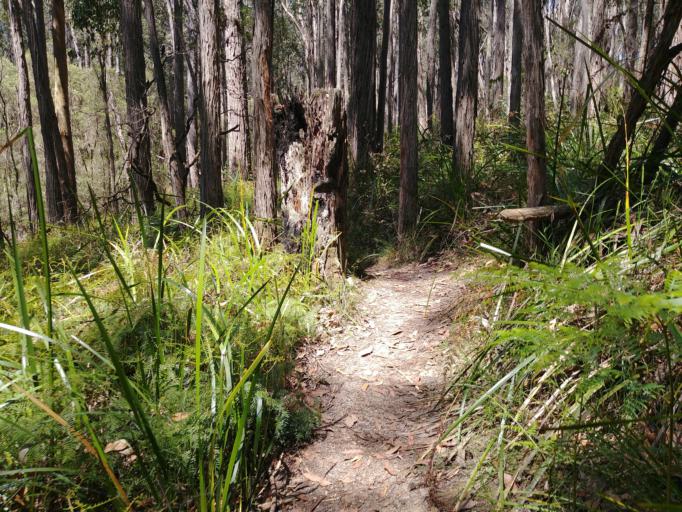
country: AU
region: Victoria
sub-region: Cardinia
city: Gembrook
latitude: -37.8988
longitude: 145.5728
